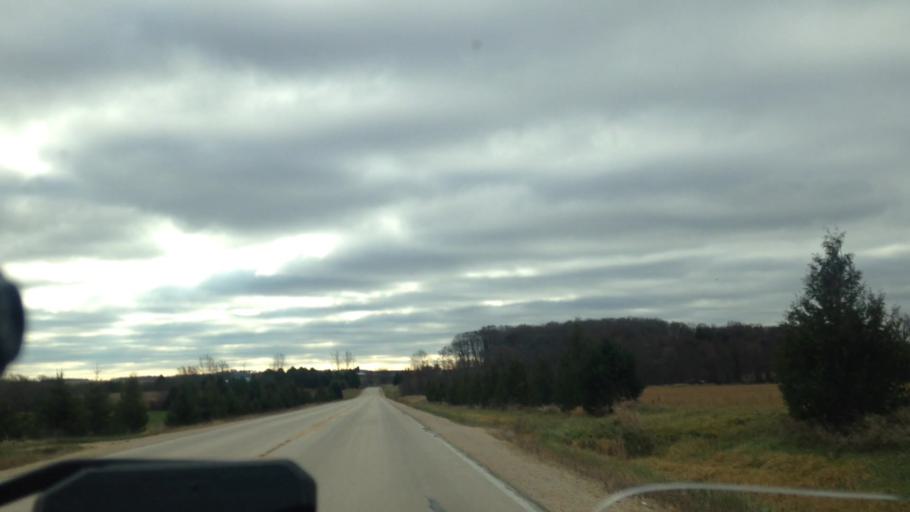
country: US
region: Wisconsin
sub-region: Dodge County
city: Mayville
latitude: 43.4846
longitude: -88.5116
